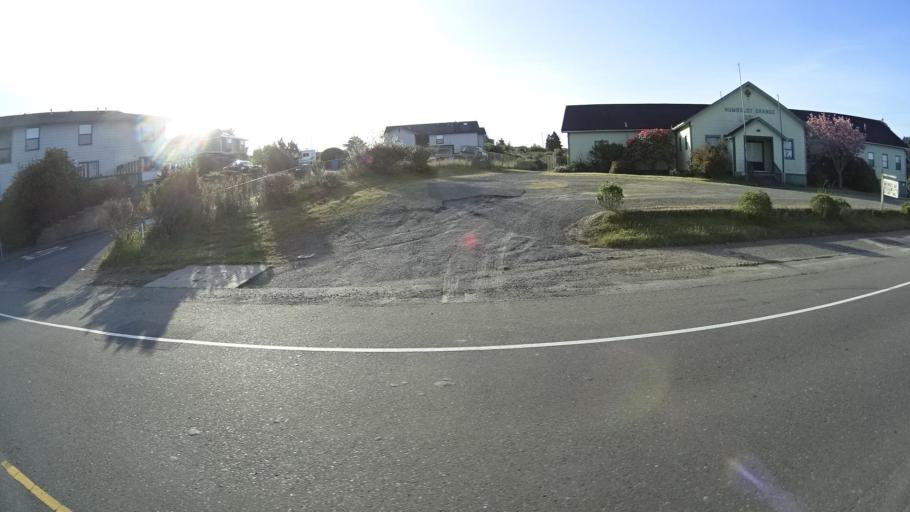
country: US
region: California
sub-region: Humboldt County
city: Humboldt Hill
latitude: 40.7392
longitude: -124.1998
